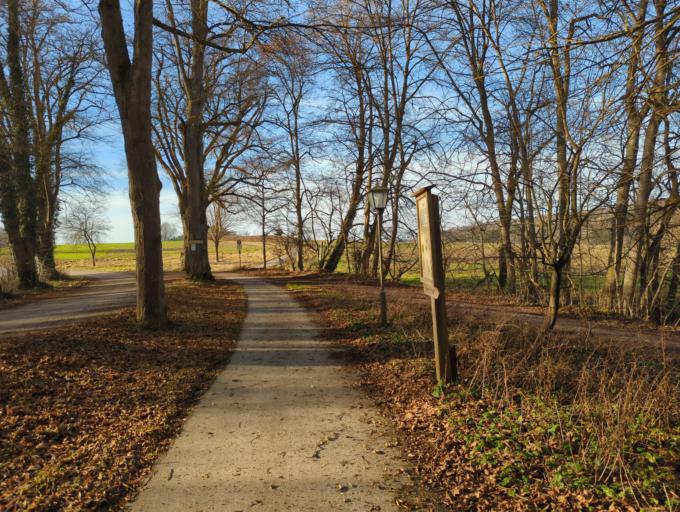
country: DE
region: Bavaria
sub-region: Swabia
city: Krumbach
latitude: 48.2463
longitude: 10.3886
